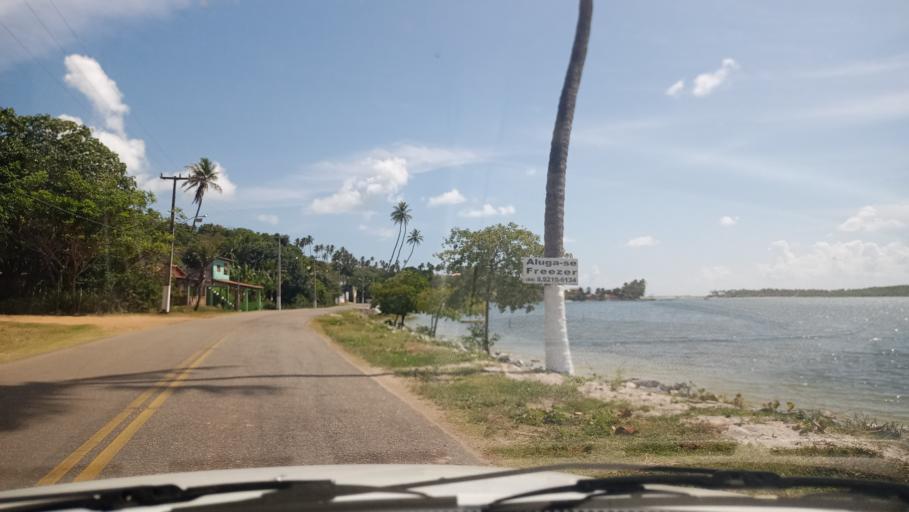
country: BR
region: Rio Grande do Norte
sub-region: Canguaretama
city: Canguaretama
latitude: -6.3232
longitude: -35.0523
